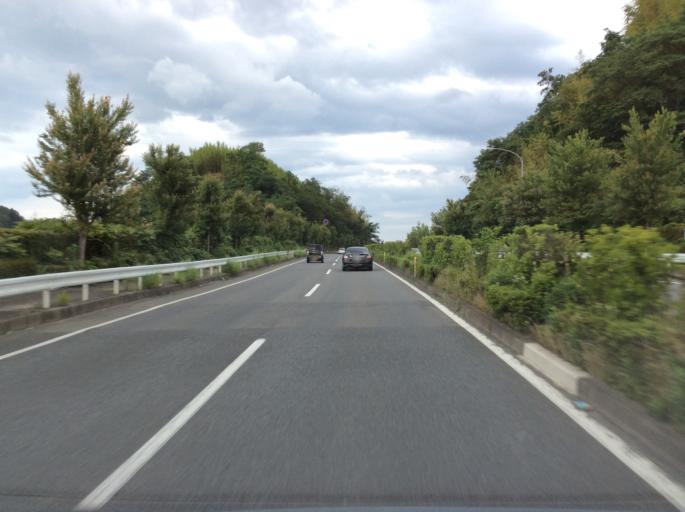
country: JP
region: Fukushima
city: Iwaki
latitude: 37.0682
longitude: 140.8449
